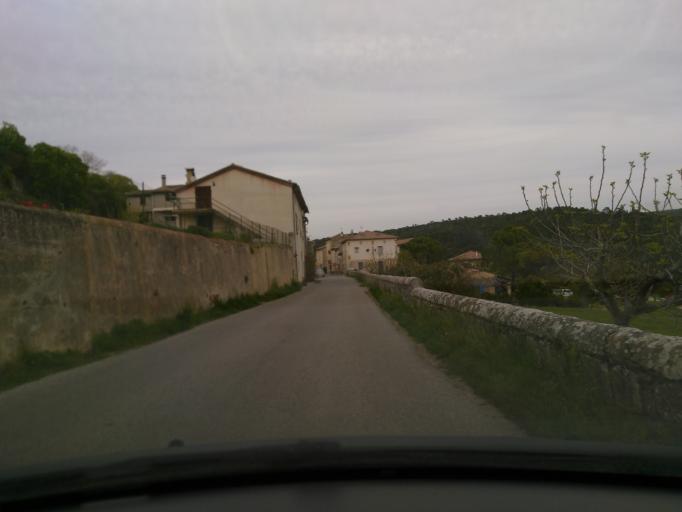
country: FR
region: Rhone-Alpes
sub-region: Departement de l'Ardeche
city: Ruoms
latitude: 44.4456
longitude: 4.4163
